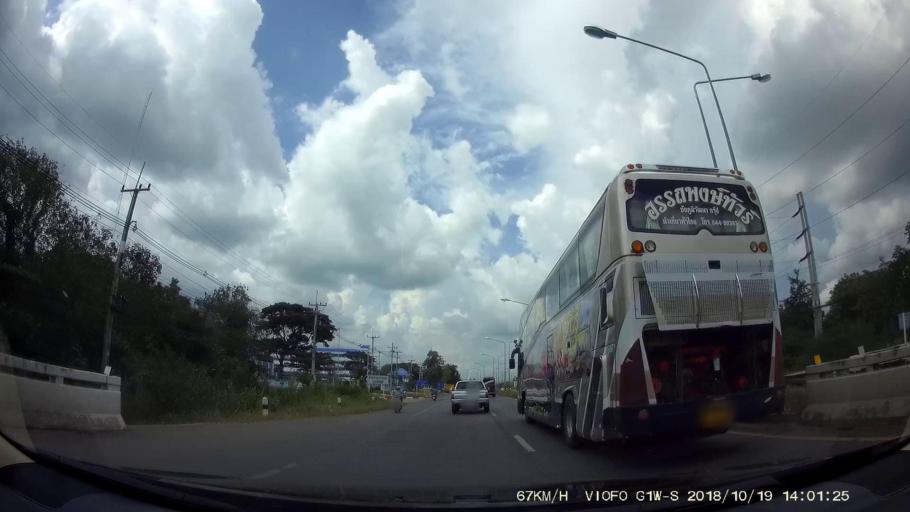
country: TH
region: Chaiyaphum
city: Chaiyaphum
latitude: 15.8291
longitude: 102.0587
